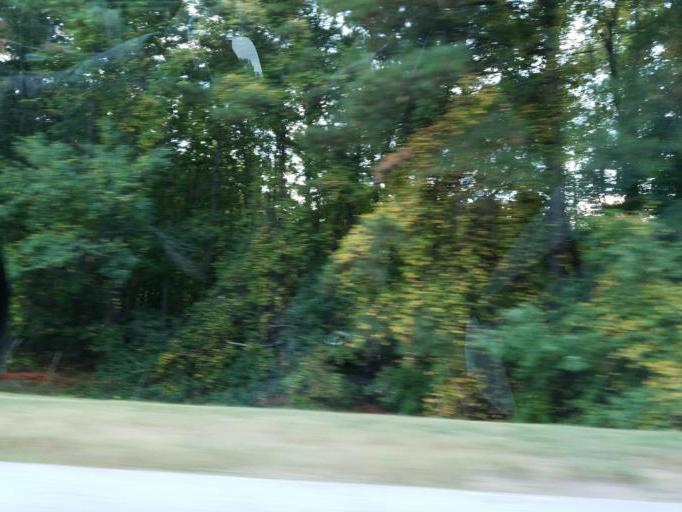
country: US
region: Georgia
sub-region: Cobb County
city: Kennesaw
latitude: 34.0479
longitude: -84.5854
